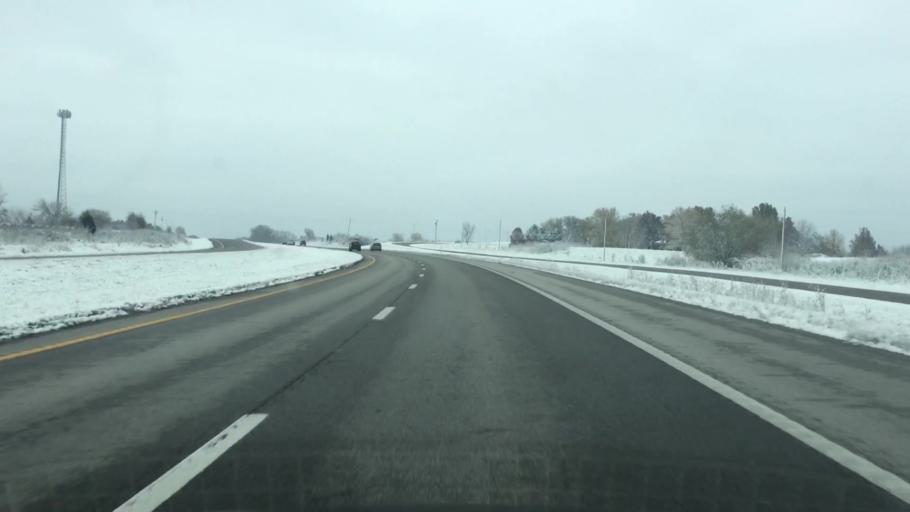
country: US
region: Missouri
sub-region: Cass County
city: Garden City
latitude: 38.5536
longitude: -94.1783
